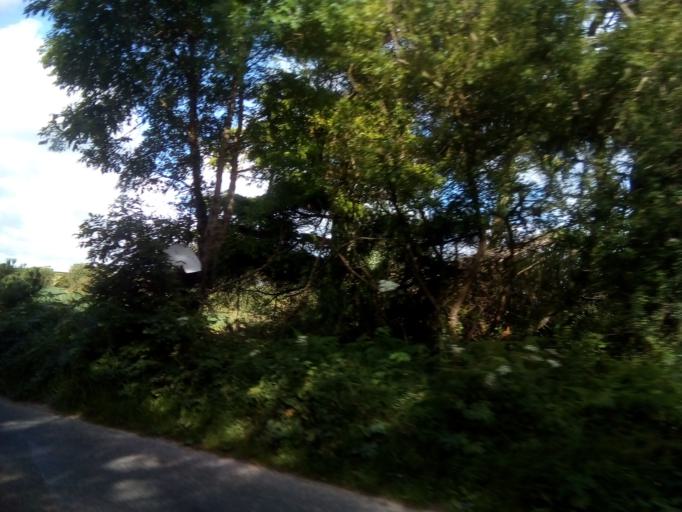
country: IE
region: Leinster
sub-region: Loch Garman
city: Loch Garman
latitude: 52.2709
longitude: -6.5501
